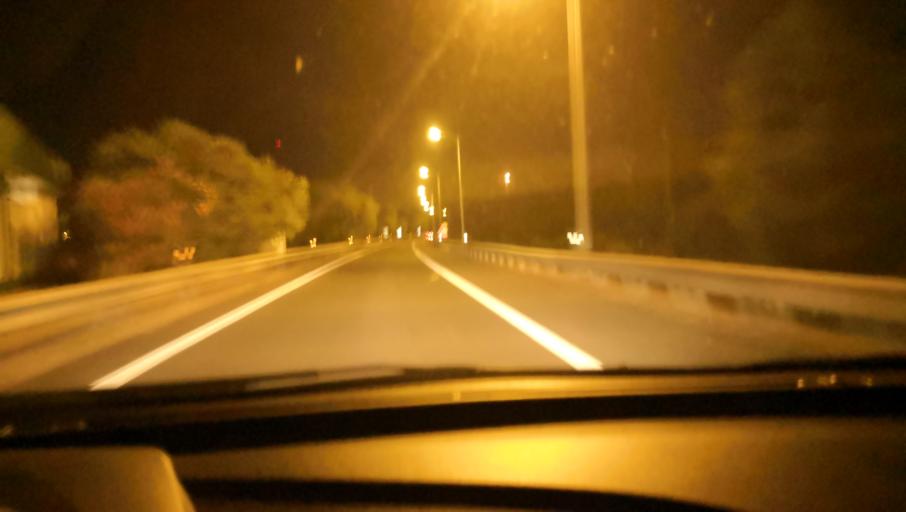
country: PT
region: Setubal
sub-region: Barreiro
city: Santo Antonio da Charneca
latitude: 38.5798
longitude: -9.0141
